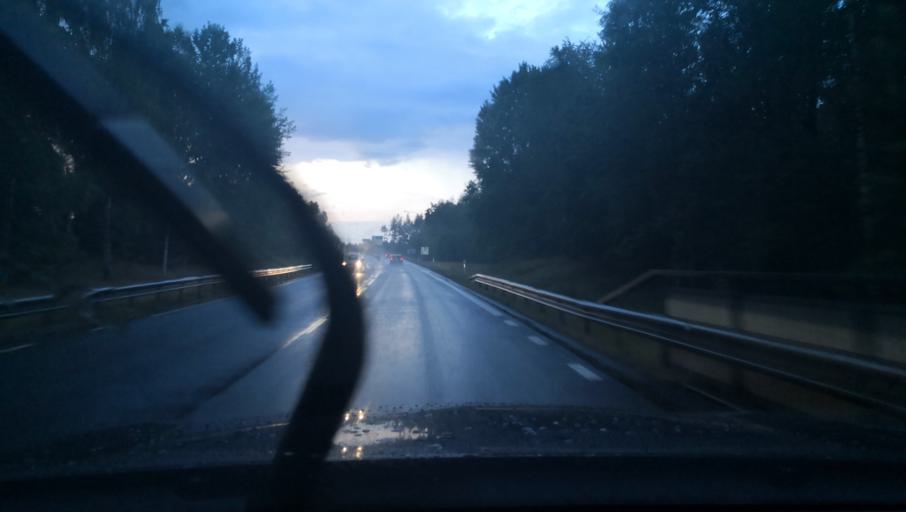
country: SE
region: Kronoberg
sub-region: Vaxjo Kommun
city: Vaexjoe
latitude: 56.8949
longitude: 14.8292
